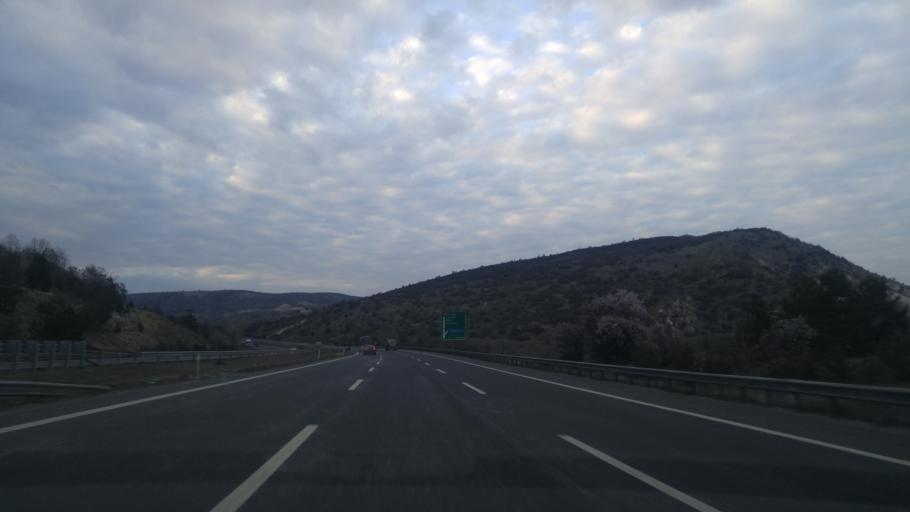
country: TR
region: Ankara
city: Camlidere
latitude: 40.4261
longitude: 32.4302
